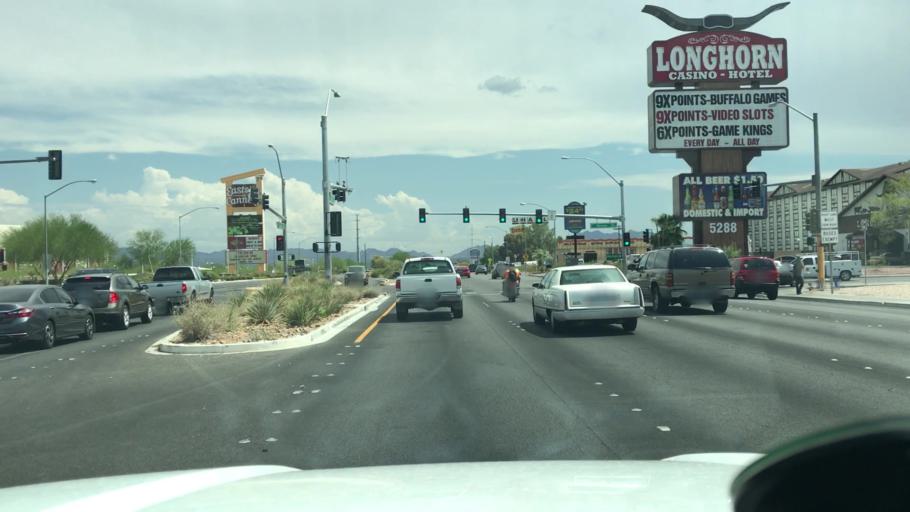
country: US
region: Nevada
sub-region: Clark County
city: Whitney
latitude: 36.1084
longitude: -115.0596
